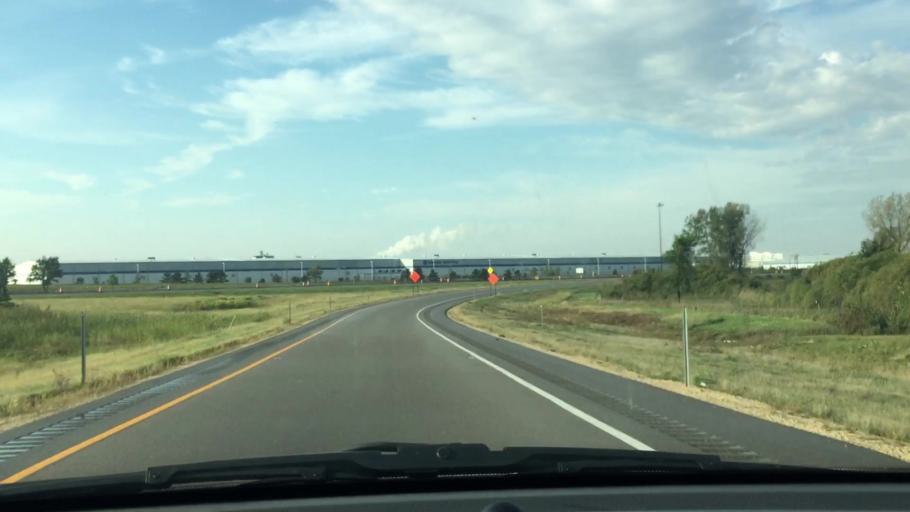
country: US
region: Illinois
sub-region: Ogle County
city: Rochelle
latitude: 41.9064
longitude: -89.0248
